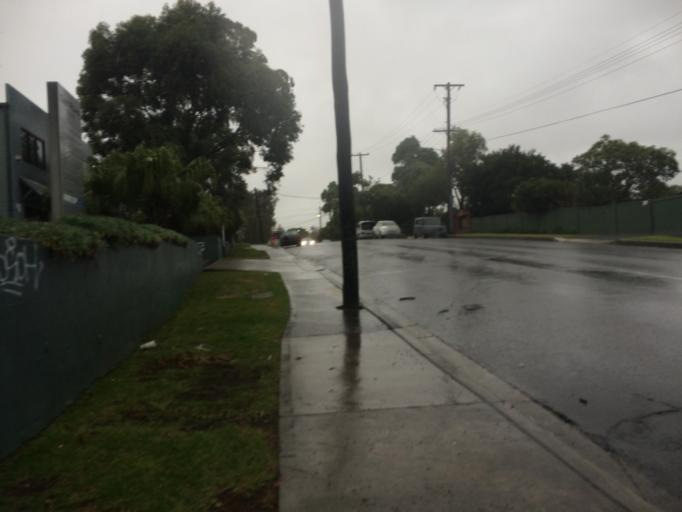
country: AU
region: New South Wales
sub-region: Sutherland Shire
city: Kirrawee
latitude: -34.0268
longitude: 151.0727
